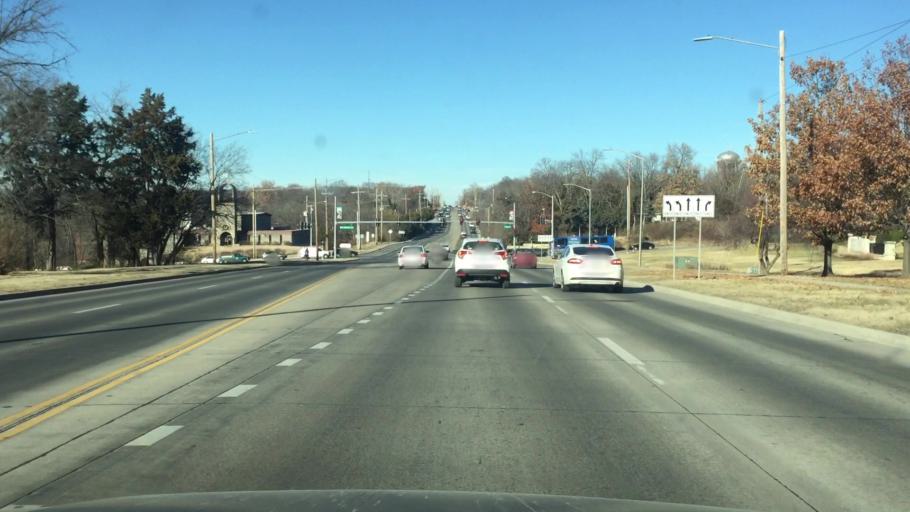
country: US
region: Kansas
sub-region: Douglas County
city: Lawrence
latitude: 38.9554
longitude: -95.2605
